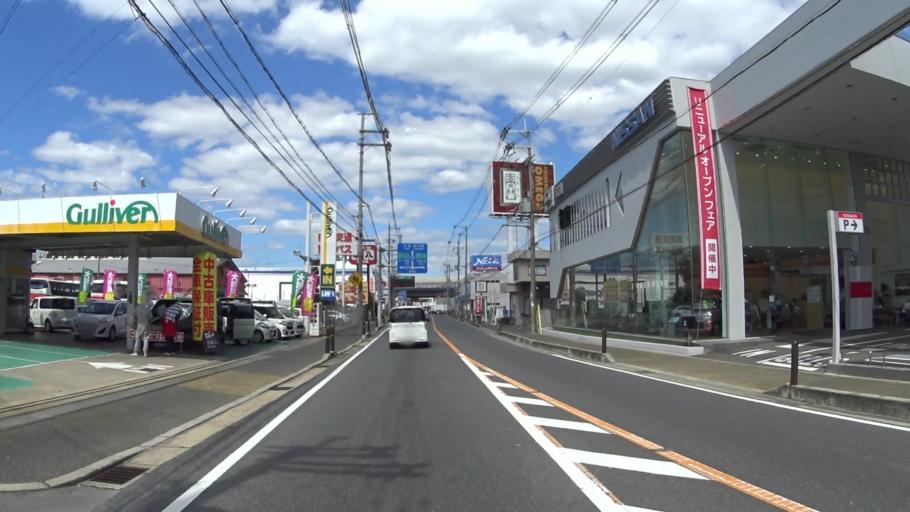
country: JP
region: Kyoto
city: Uji
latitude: 34.9064
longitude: 135.7838
